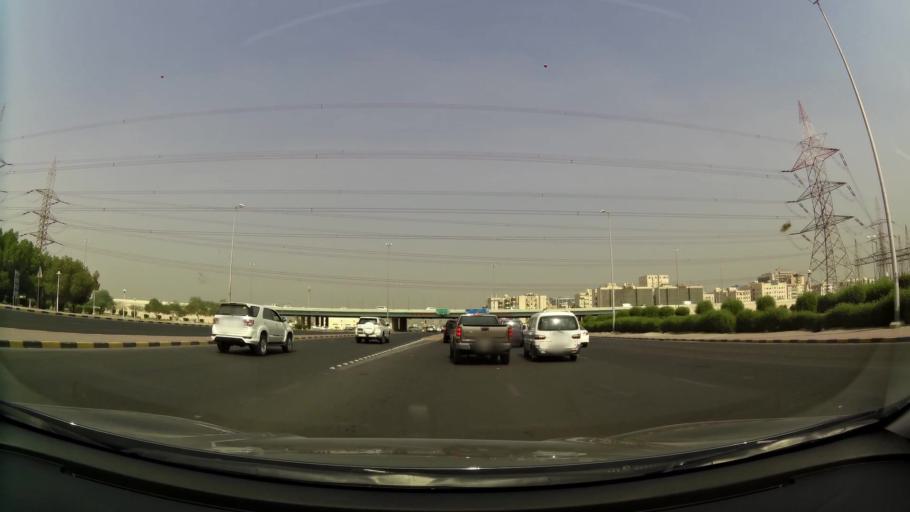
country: KW
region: Al Asimah
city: Ar Rabiyah
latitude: 29.2970
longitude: 47.9056
